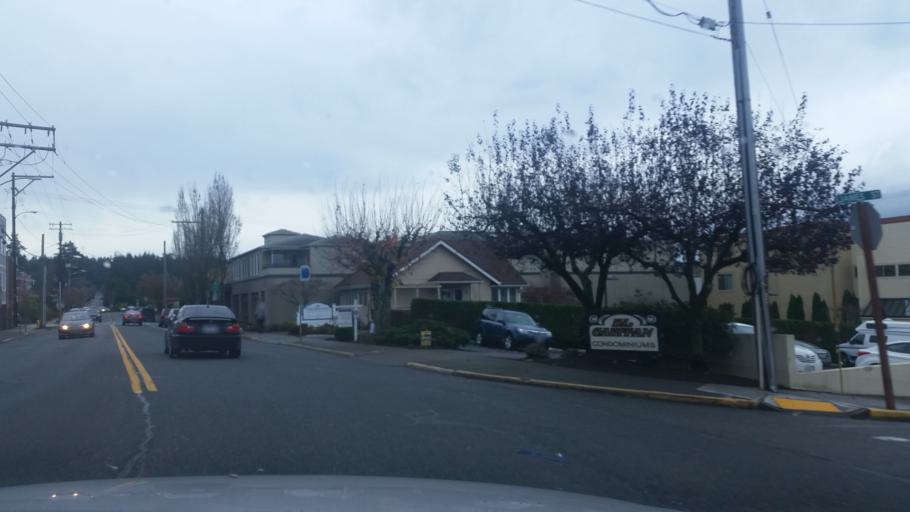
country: US
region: Washington
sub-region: Snohomish County
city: Edmonds
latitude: 47.8106
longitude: -122.3803
